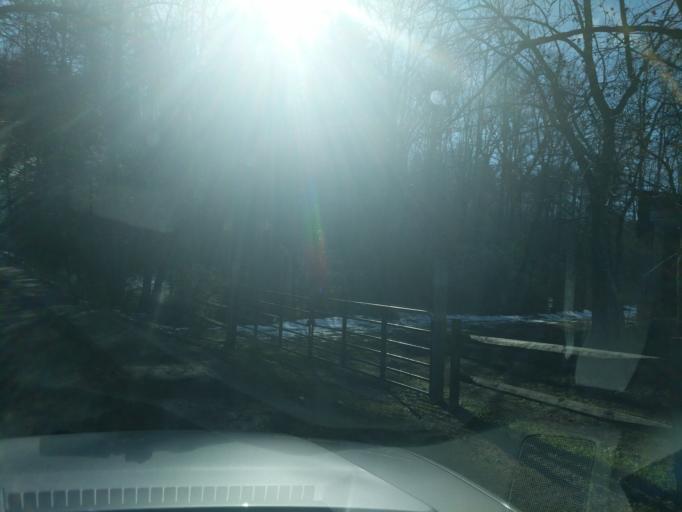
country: US
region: North Carolina
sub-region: McDowell County
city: West Marion
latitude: 35.5975
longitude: -81.9807
